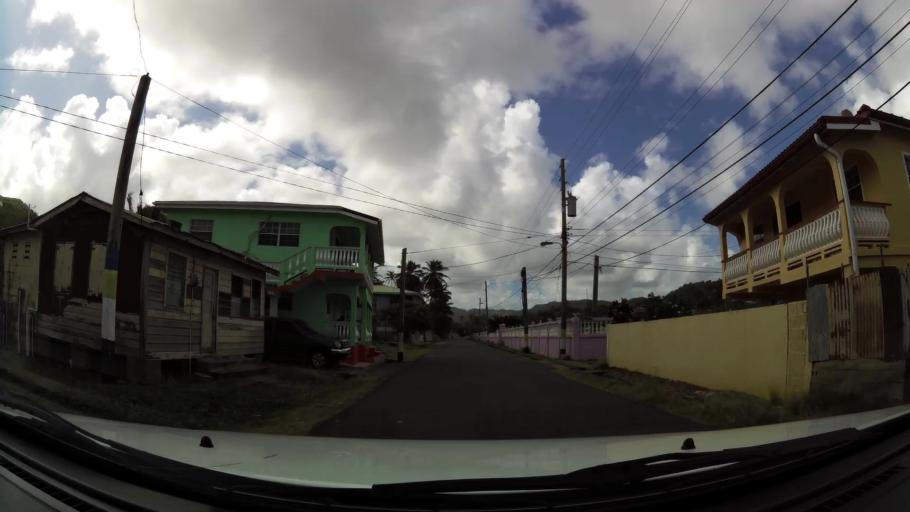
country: LC
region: Dennery Quarter
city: Dennery
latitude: 13.9086
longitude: -60.8925
